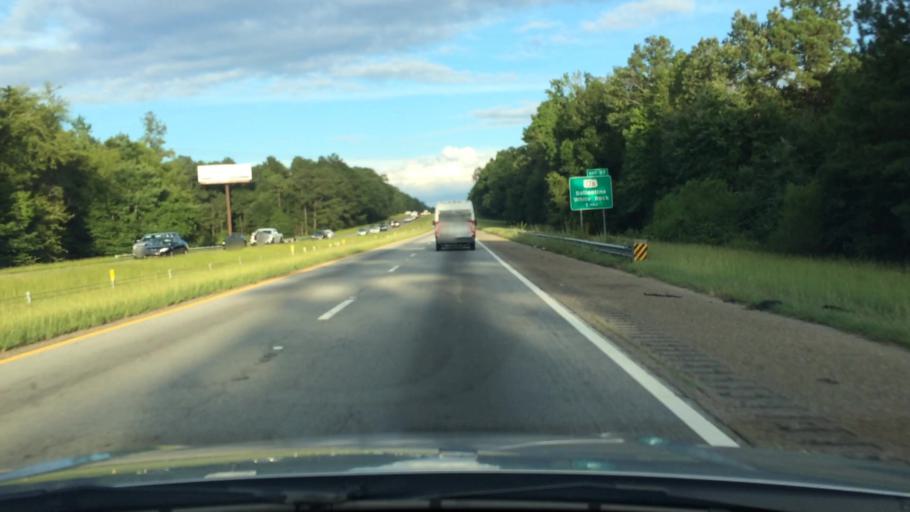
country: US
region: South Carolina
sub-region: Richland County
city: Lake Murray of Richland
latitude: 34.1532
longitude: -81.2561
